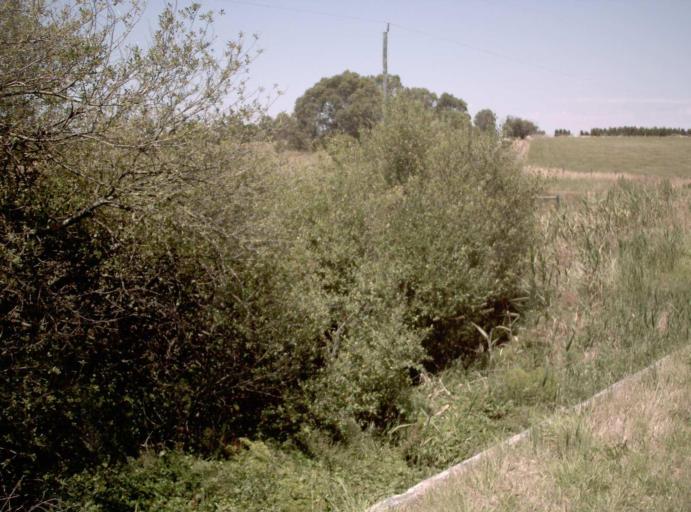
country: AU
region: Victoria
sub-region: Bass Coast
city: North Wonthaggi
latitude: -38.6141
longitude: 145.9690
